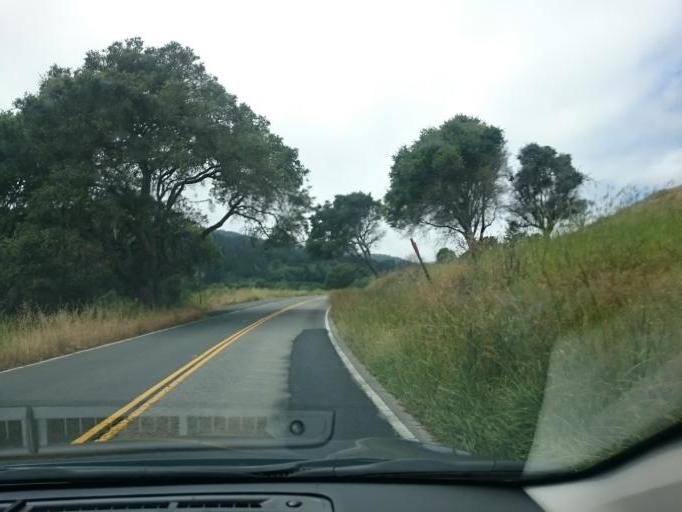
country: US
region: California
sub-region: Marin County
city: Bolinas
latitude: 37.9472
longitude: -122.7098
